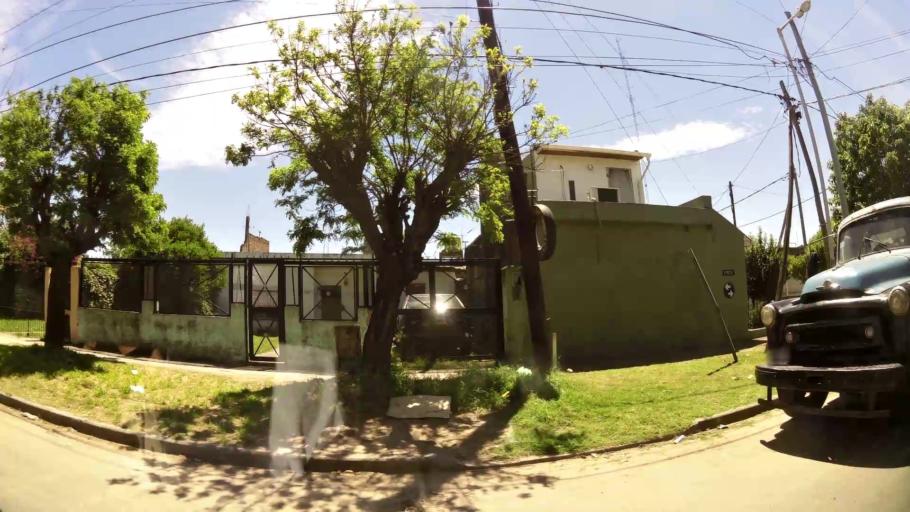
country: AR
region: Buenos Aires
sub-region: Partido de Lanus
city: Lanus
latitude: -34.7213
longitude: -58.3272
